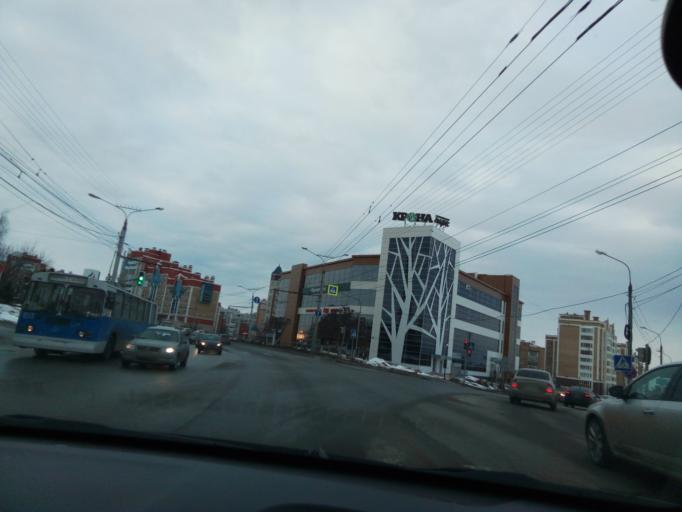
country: RU
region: Chuvashia
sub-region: Cheboksarskiy Rayon
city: Cheboksary
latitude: 56.1480
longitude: 47.2016
